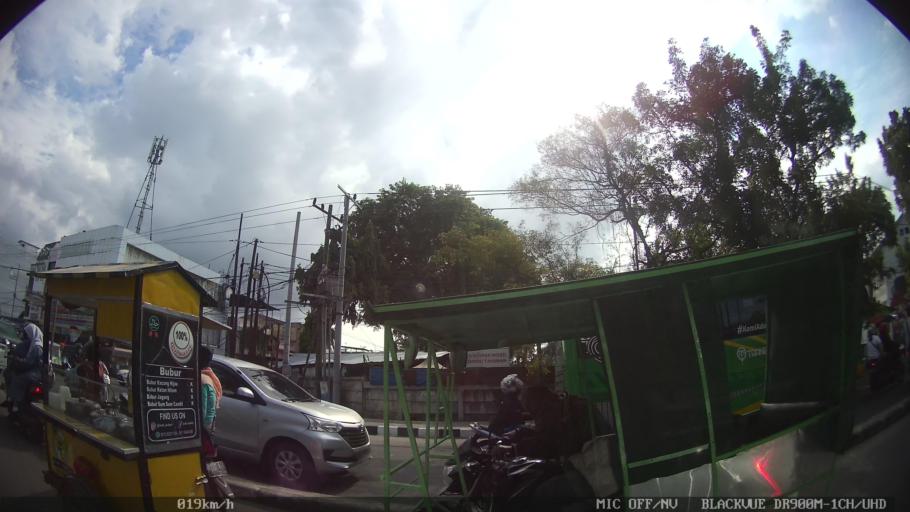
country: ID
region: North Sumatra
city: Medan
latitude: 3.6208
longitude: 98.6709
